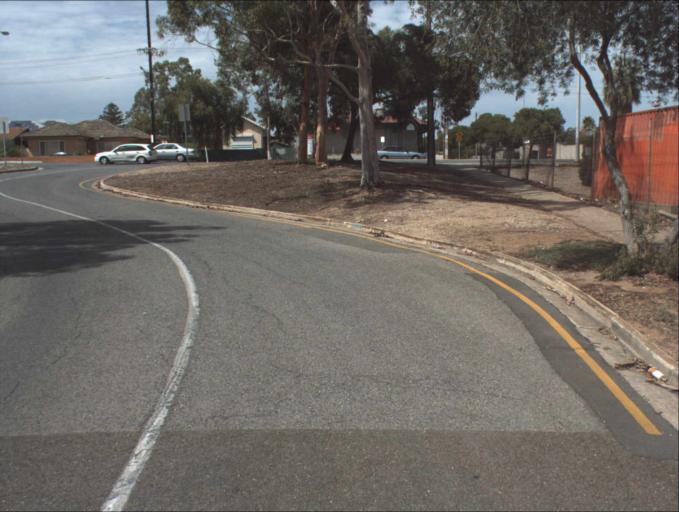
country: AU
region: South Australia
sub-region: Salisbury
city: Ingle Farm
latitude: -34.8468
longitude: 138.6226
